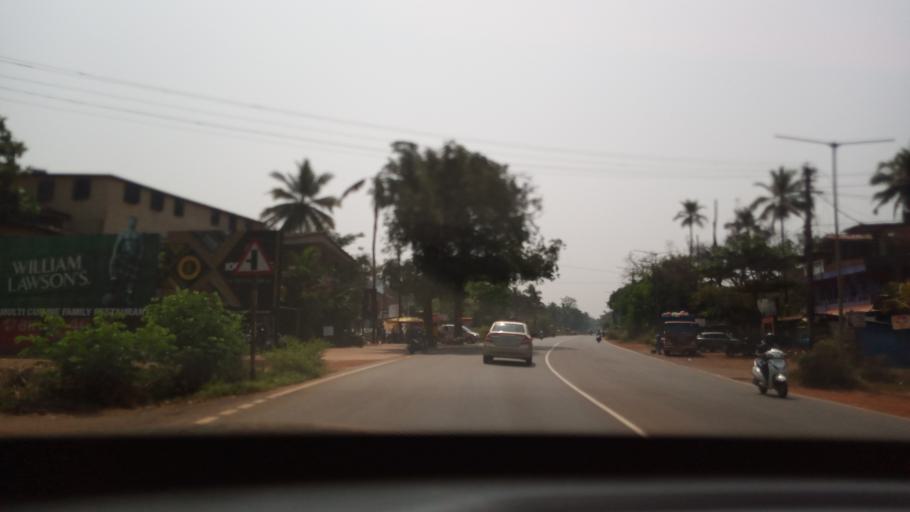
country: IN
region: Goa
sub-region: South Goa
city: Raia
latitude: 15.3213
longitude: 73.9408
